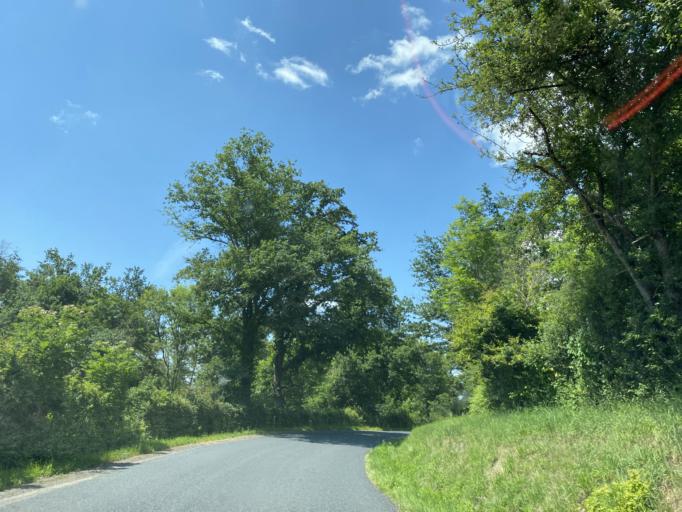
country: FR
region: Auvergne
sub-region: Departement du Puy-de-Dome
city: Courpiere
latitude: 45.7779
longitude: 3.5497
